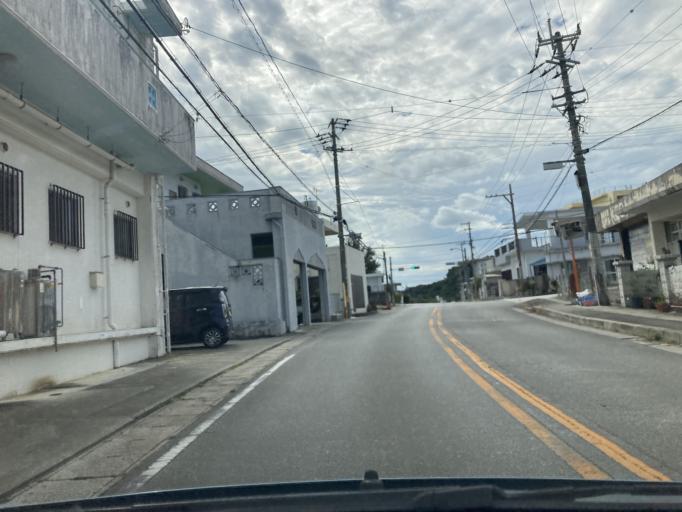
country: JP
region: Okinawa
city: Ishikawa
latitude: 26.4340
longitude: 127.7781
